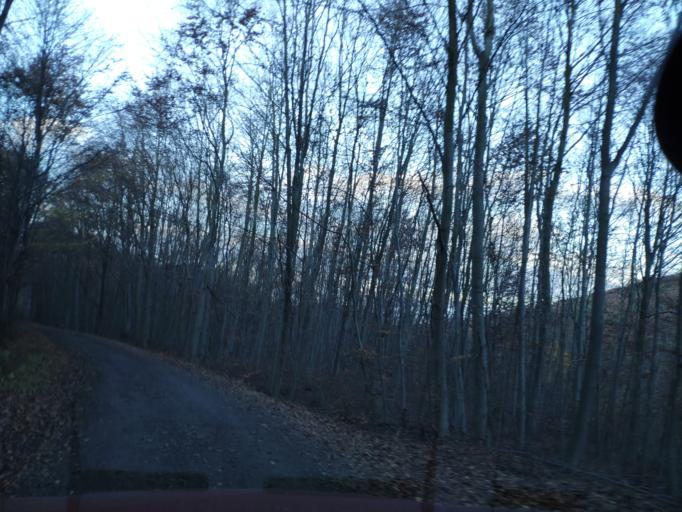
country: SK
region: Kosicky
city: Secovce
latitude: 48.5992
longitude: 21.5131
